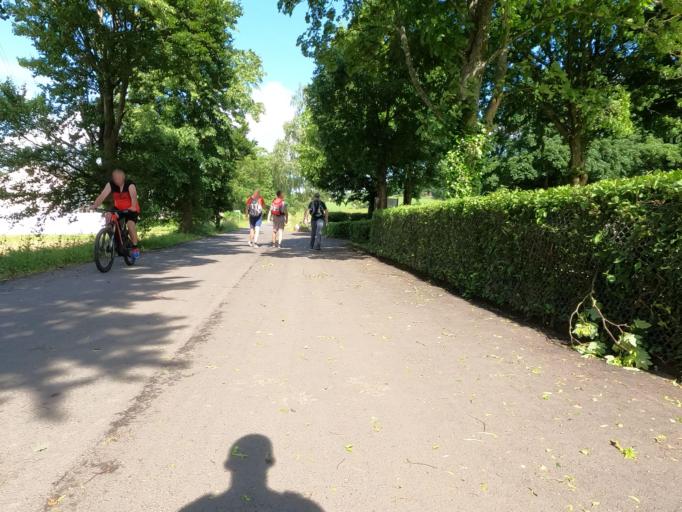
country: DE
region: Rheinland-Pfalz
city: Nister
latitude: 50.6766
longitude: 7.8277
